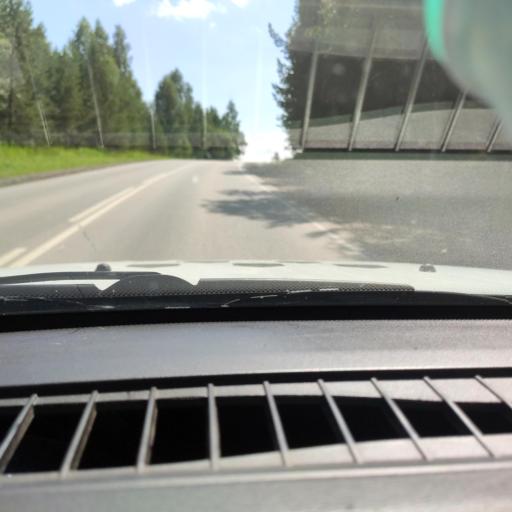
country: RU
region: Bashkortostan
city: Mesyagutovo
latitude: 55.5042
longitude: 58.3225
